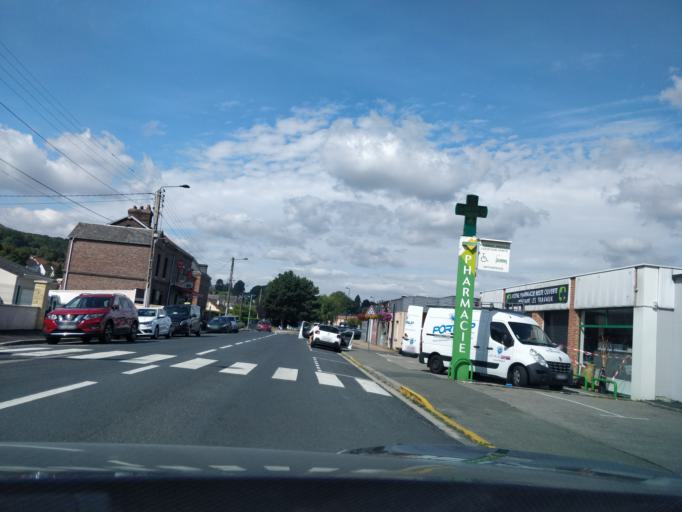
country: FR
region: Haute-Normandie
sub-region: Departement de la Seine-Maritime
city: Saint-Leger-du-Bourg-Denis
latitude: 49.4317
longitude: 1.1592
